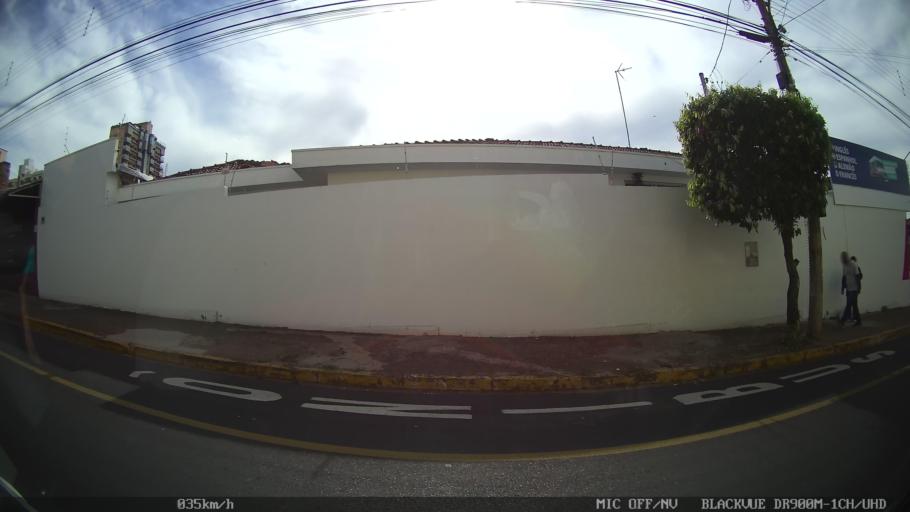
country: BR
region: Sao Paulo
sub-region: Catanduva
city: Catanduva
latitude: -21.1391
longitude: -48.9716
